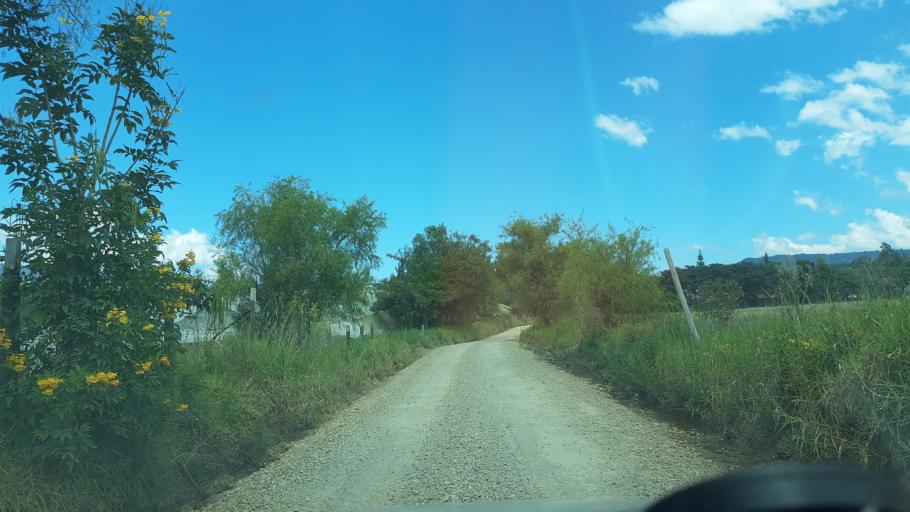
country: CO
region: Boyaca
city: Villa de Leiva
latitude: 5.6593
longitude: -73.5728
